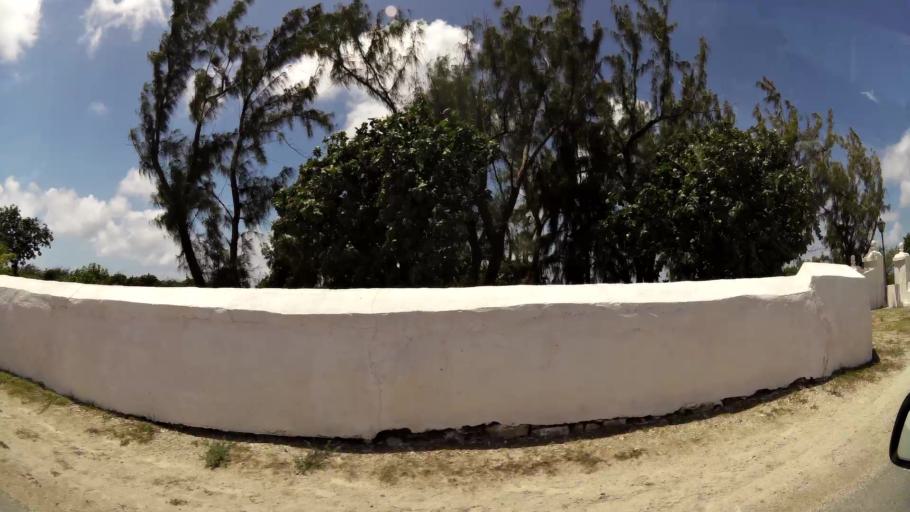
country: TC
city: Cockburn Town
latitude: 21.4395
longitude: -71.1475
